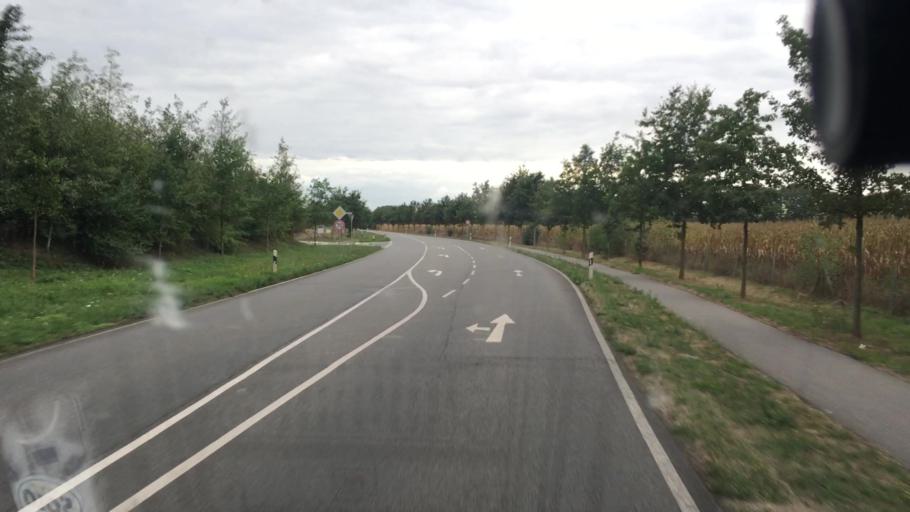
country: DE
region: Lower Saxony
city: Lohne
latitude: 52.6497
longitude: 8.2191
